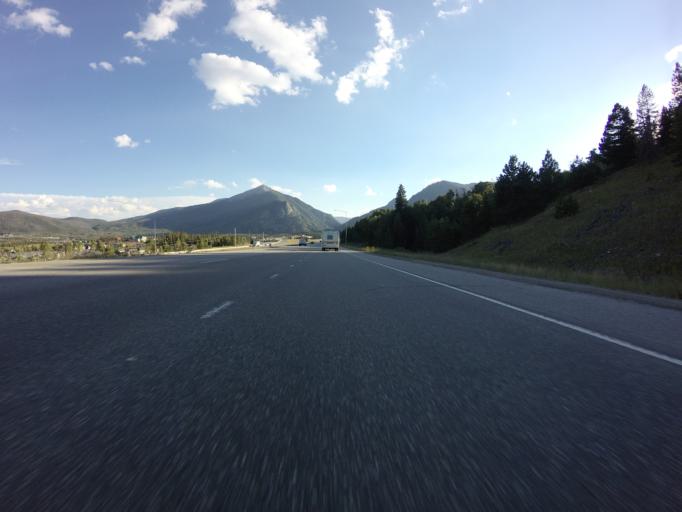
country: US
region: Colorado
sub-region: Summit County
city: Frisco
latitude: 39.5969
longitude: -106.0930
